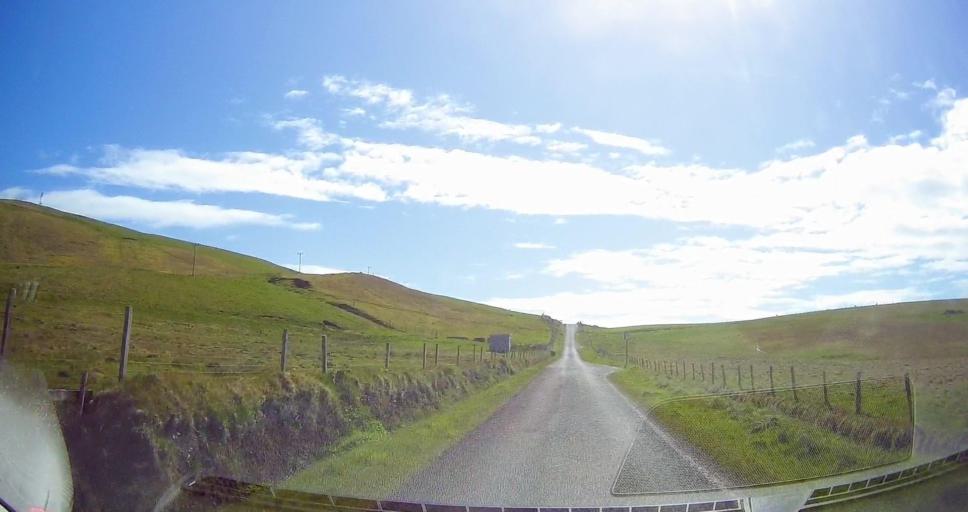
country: GB
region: Scotland
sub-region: Shetland Islands
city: Sandwick
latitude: 59.9639
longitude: -1.3220
